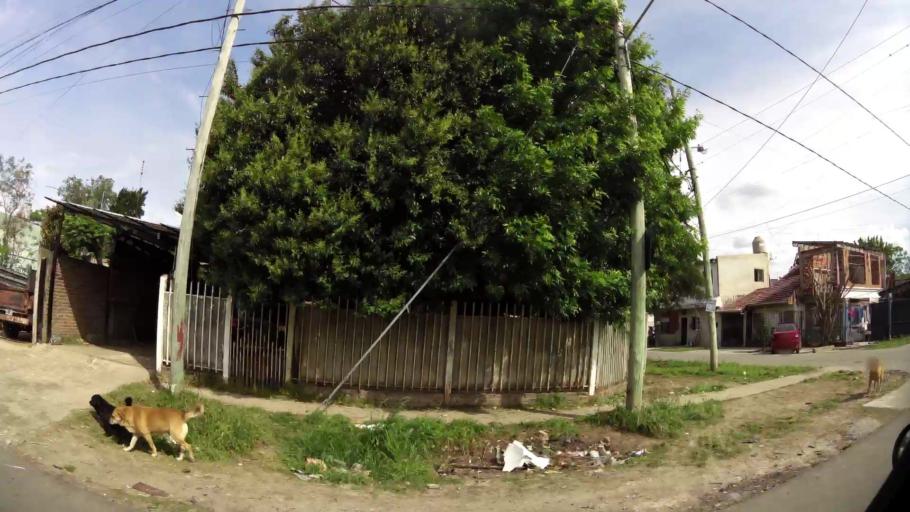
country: AR
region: Buenos Aires
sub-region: Partido de Quilmes
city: Quilmes
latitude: -34.7662
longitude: -58.2441
